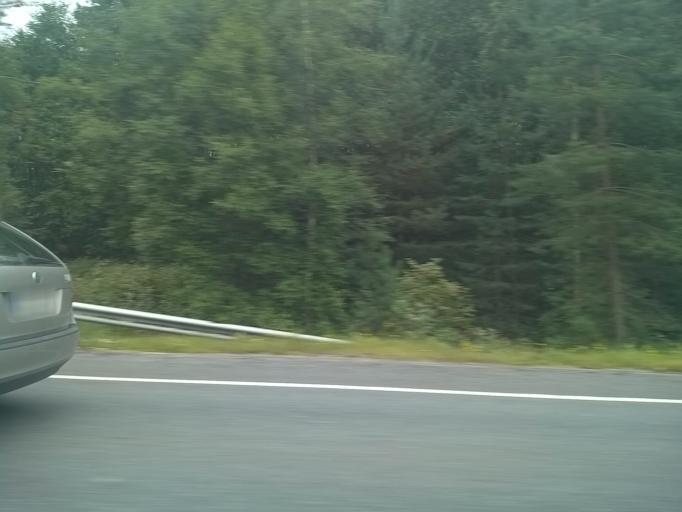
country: FI
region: Pirkanmaa
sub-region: Tampere
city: Tampere
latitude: 61.4860
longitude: 23.8266
